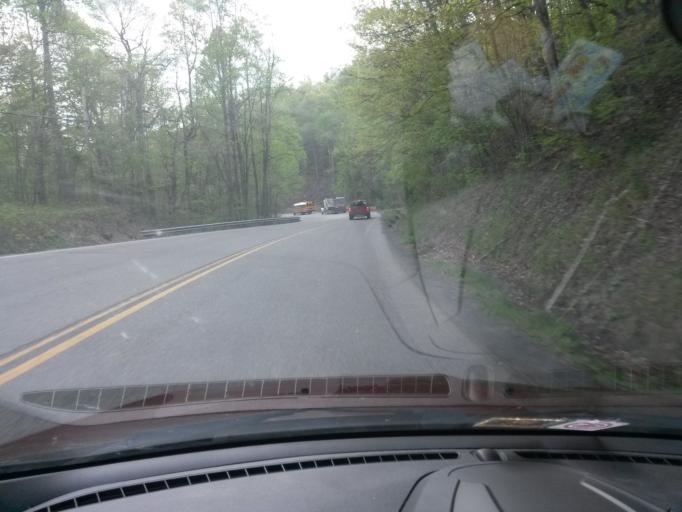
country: US
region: West Virginia
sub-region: Greenbrier County
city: Rainelle
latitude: 38.0225
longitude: -80.7257
